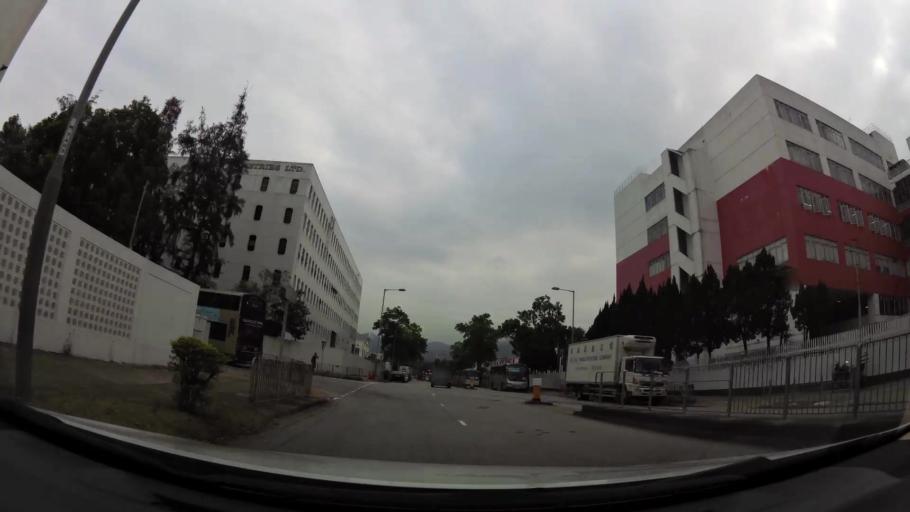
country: HK
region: Tai Po
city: Tai Po
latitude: 22.4584
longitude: 114.1814
